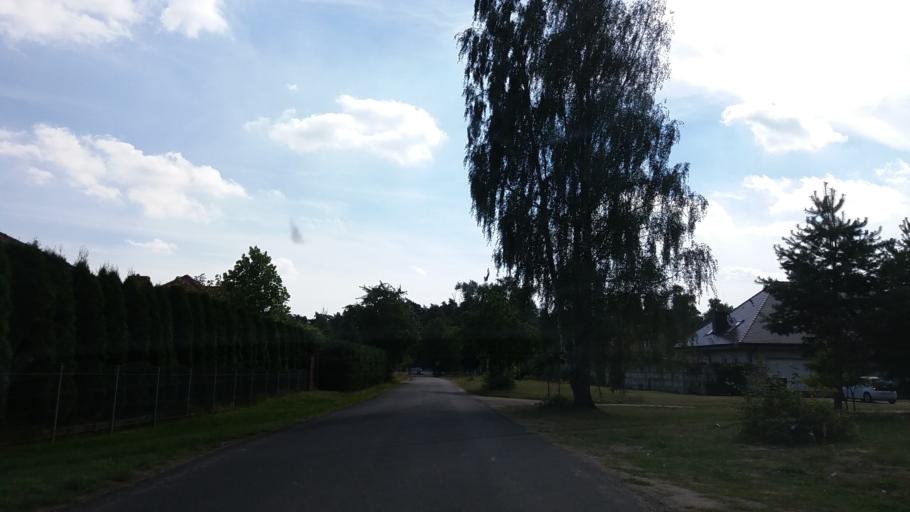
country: PL
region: West Pomeranian Voivodeship
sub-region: Powiat stargardzki
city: Kobylanka
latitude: 53.3536
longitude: 14.9083
